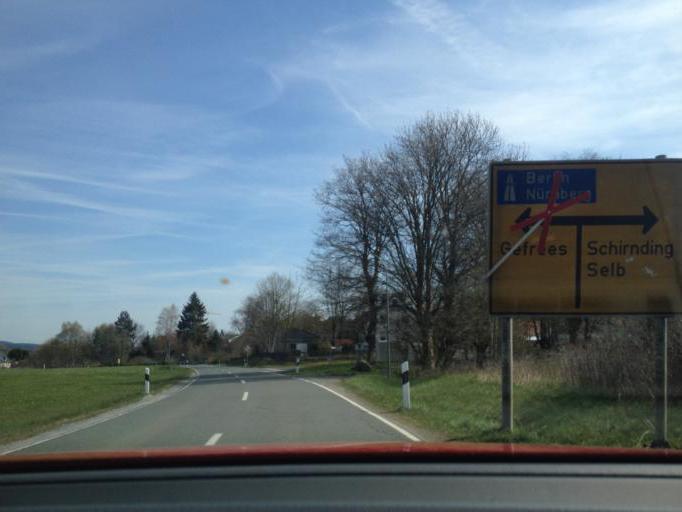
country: DE
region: Bavaria
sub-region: Upper Franconia
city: Weissenstadt
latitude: 50.0937
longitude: 11.8764
